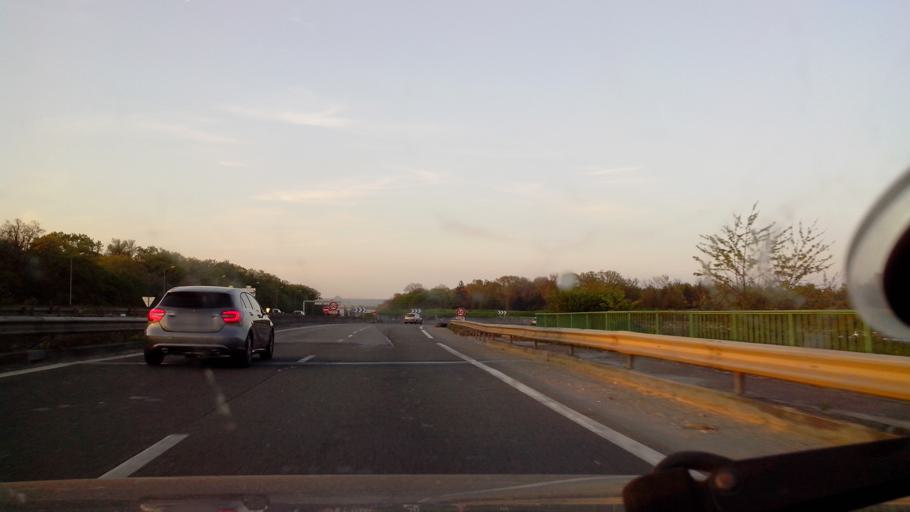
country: FR
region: Ile-de-France
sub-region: Departement de Seine-et-Marne
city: Lognes
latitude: 48.8298
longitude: 2.6192
